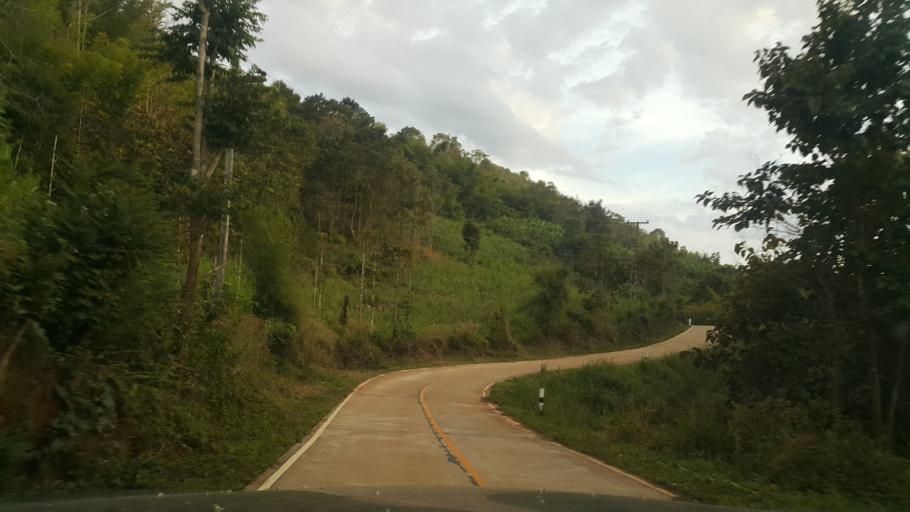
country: TH
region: Chiang Mai
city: Samoeng
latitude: 18.9915
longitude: 98.6753
